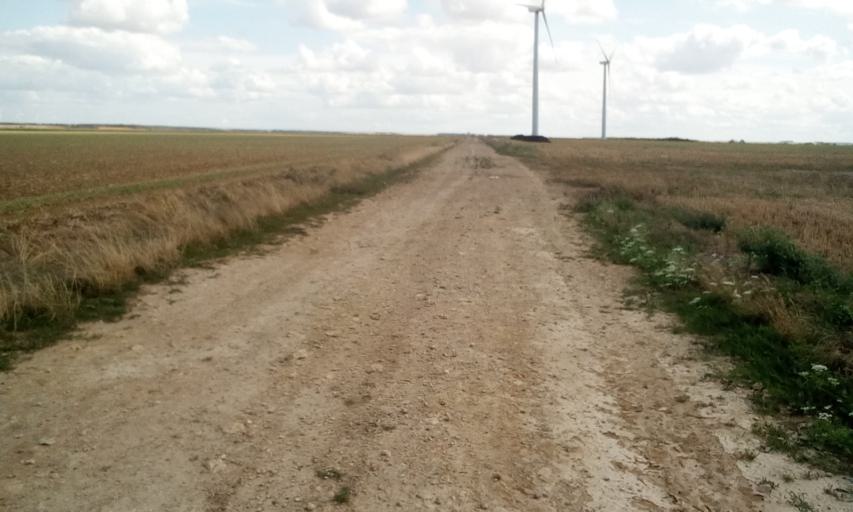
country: FR
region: Lower Normandy
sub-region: Departement du Calvados
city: Bellengreville
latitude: 49.0990
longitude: -0.2289
